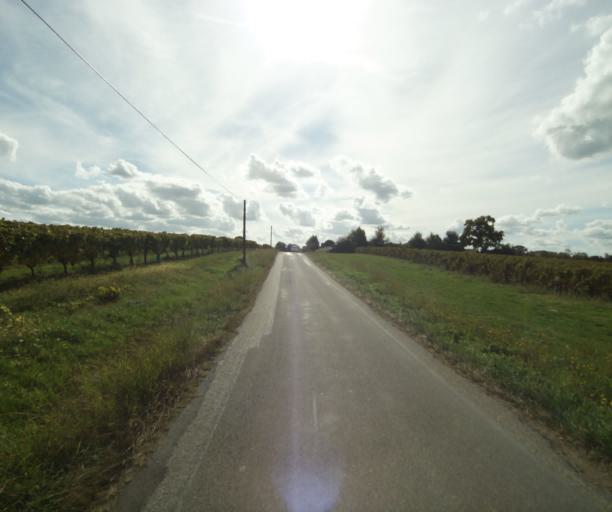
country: FR
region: Midi-Pyrenees
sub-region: Departement du Gers
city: Eauze
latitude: 43.8461
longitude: 0.1543
